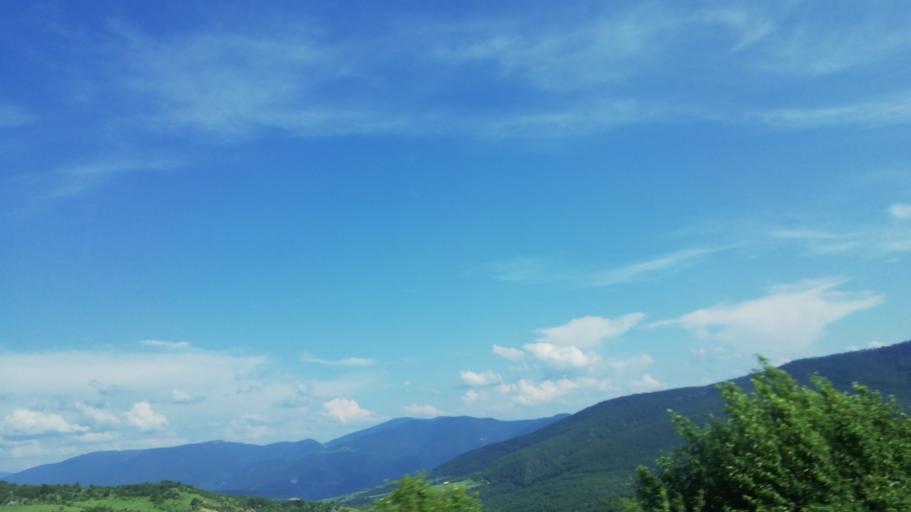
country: TR
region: Karabuk
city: Karabuk
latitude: 41.1047
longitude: 32.5962
